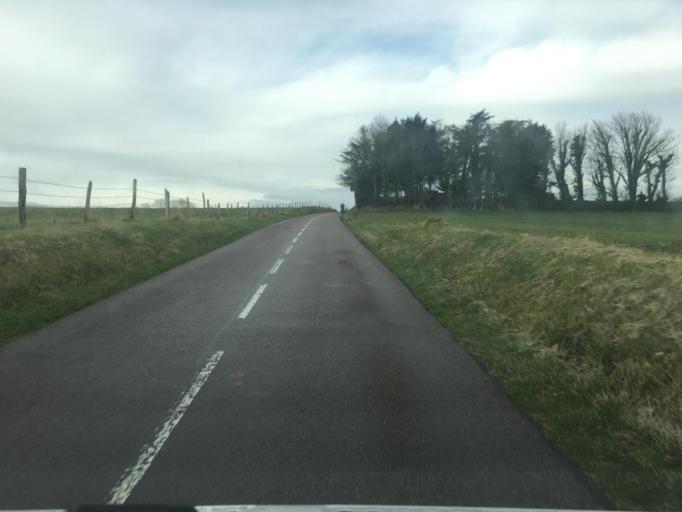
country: FR
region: Lower Normandy
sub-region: Departement du Calvados
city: Ver-sur-Mer
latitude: 49.3332
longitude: -0.6123
